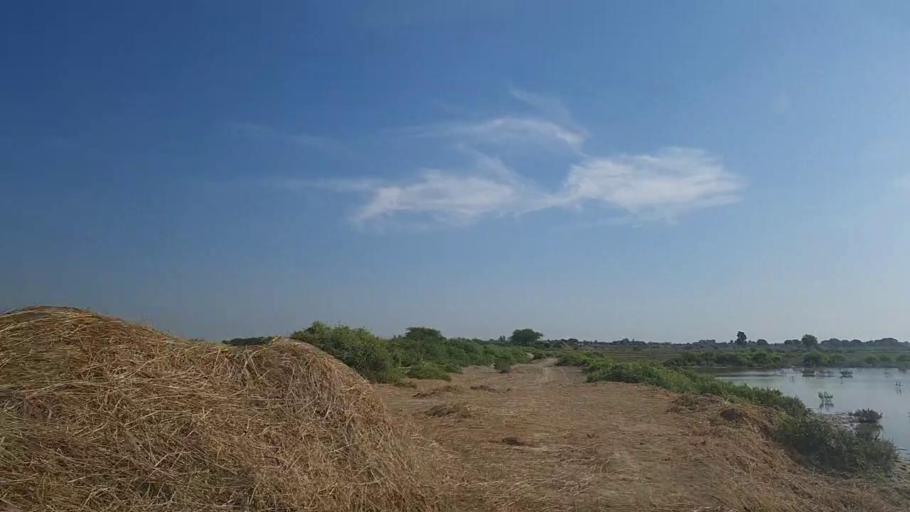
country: PK
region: Sindh
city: Mirpur Batoro
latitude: 24.7534
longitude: 68.3064
